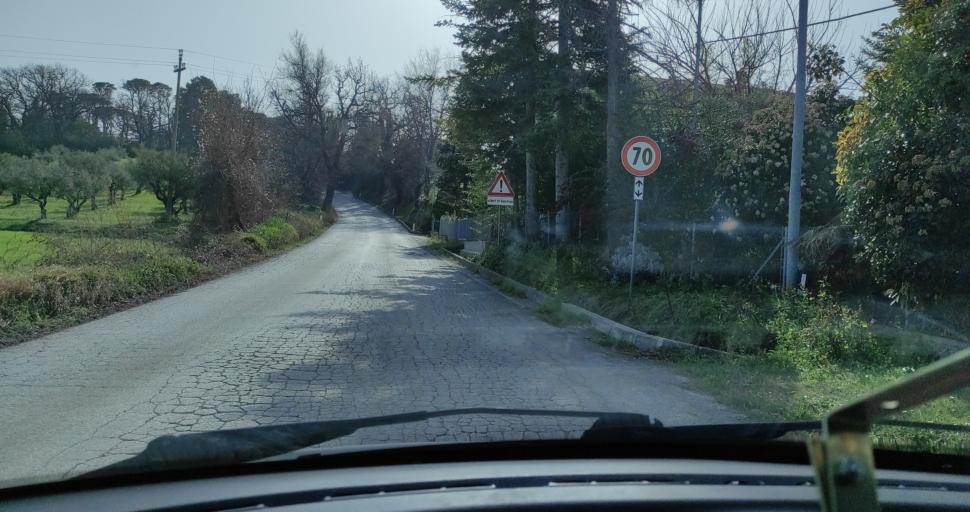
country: IT
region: The Marches
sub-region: Provincia di Macerata
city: Loro Piceno
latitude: 43.1708
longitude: 13.3974
